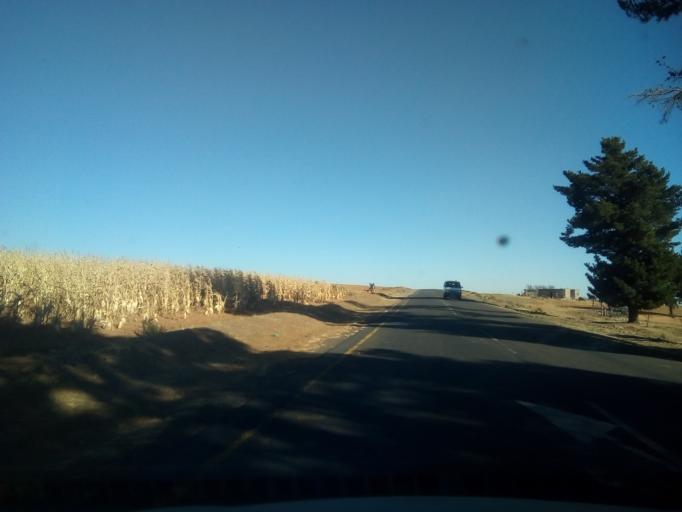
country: LS
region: Maseru
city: Maseru
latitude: -29.2931
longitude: 27.6300
